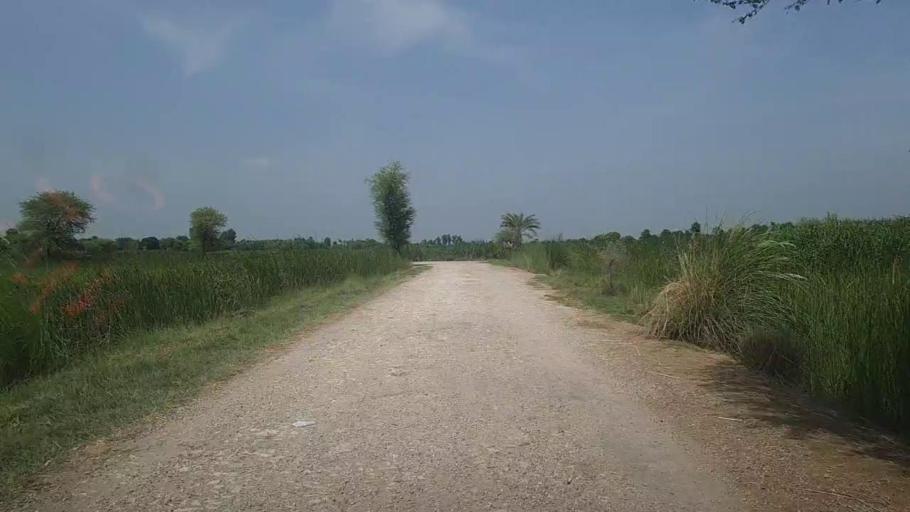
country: PK
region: Sindh
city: Ubauro
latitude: 28.1612
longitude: 69.8285
